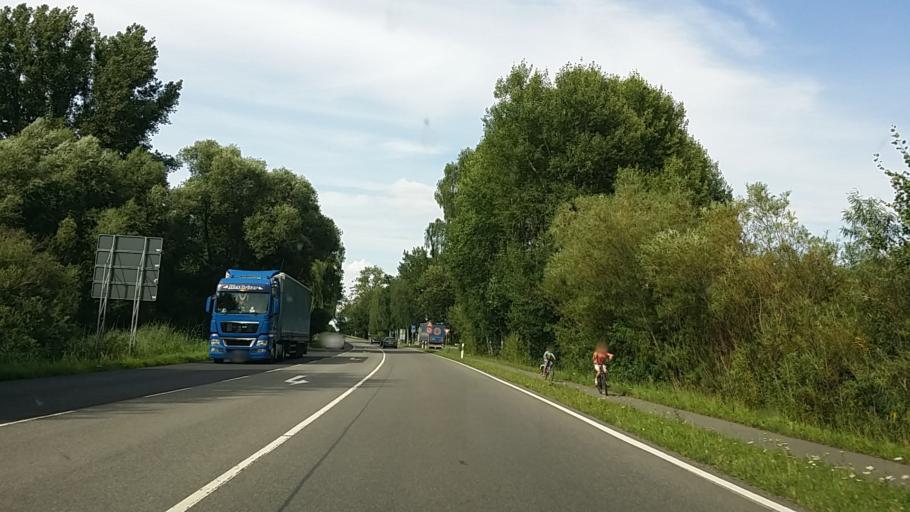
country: DE
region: Brandenburg
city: Wittenberge
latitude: 52.9708
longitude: 11.7347
